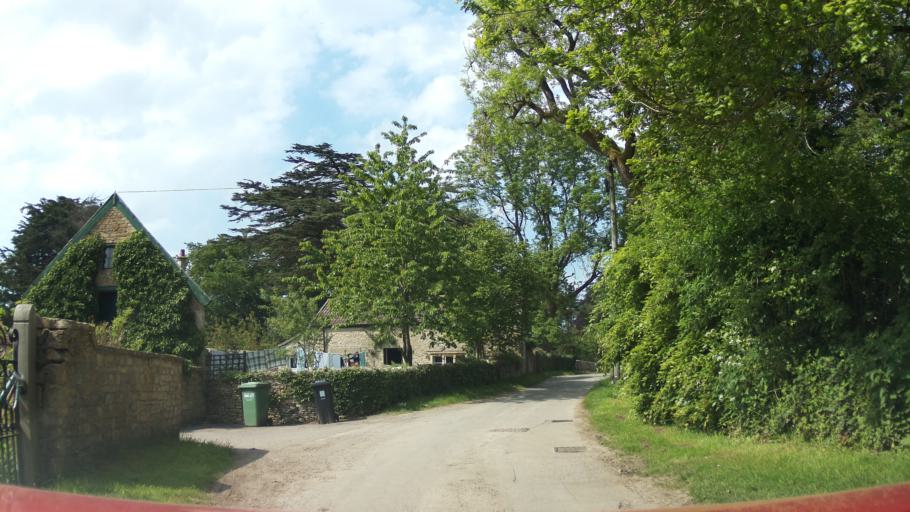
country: GB
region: England
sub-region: South Gloucestershire
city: Horton
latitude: 51.5457
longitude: -2.3514
